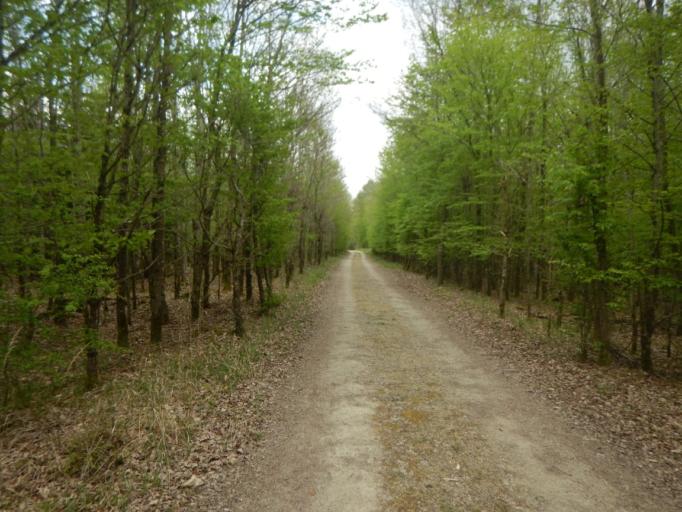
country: LU
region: Grevenmacher
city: Gonderange
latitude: 49.6861
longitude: 6.2695
